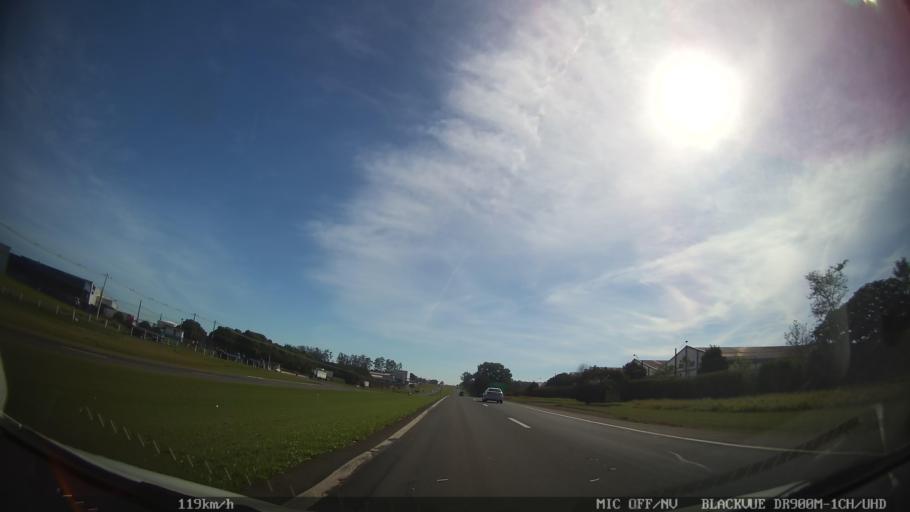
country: BR
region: Sao Paulo
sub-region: Leme
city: Leme
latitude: -22.2125
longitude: -47.3936
